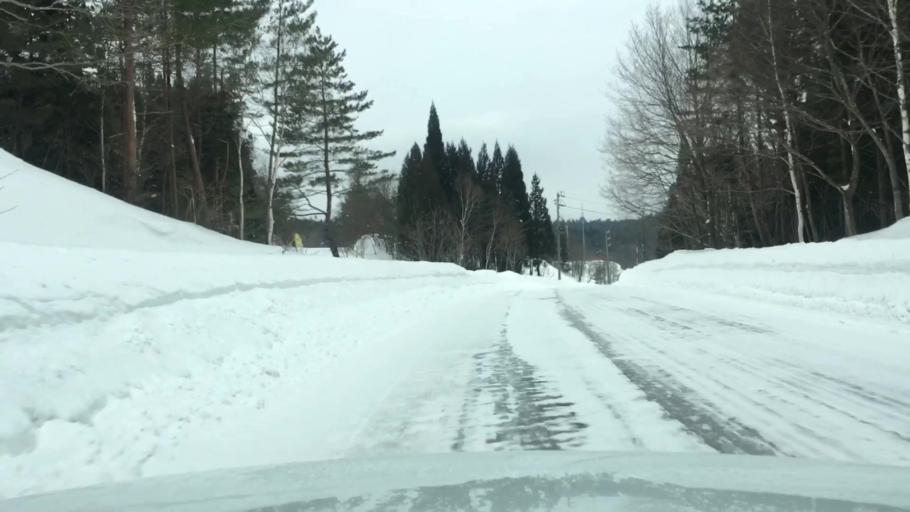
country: JP
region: Akita
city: Hanawa
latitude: 39.9900
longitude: 140.9964
